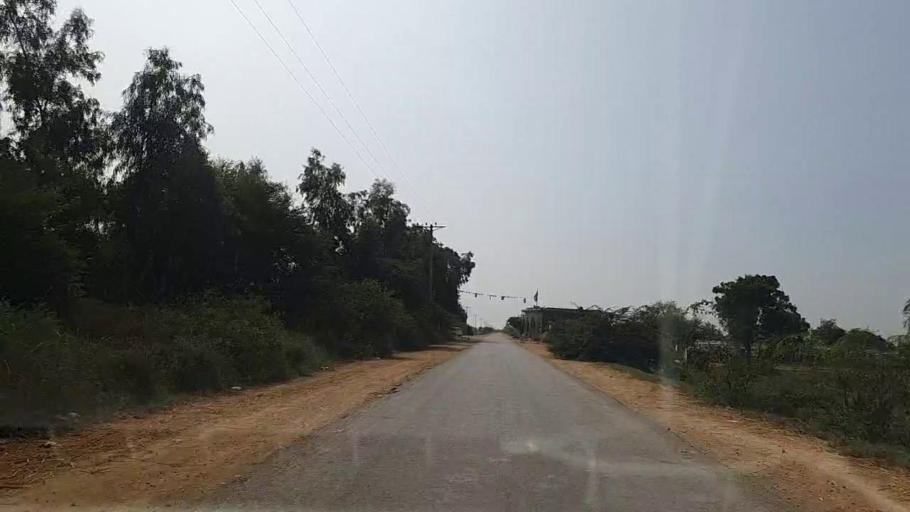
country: PK
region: Sindh
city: Chuhar Jamali
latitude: 24.3586
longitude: 67.9587
